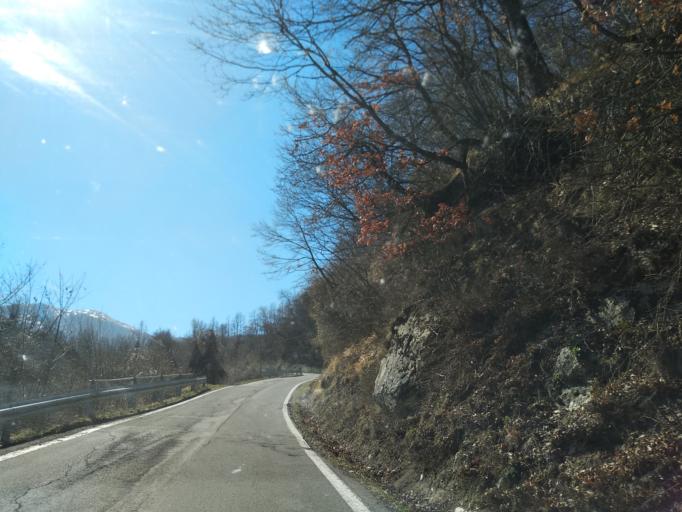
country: IT
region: Emilia-Romagna
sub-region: Provincia di Reggio Emilia
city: Ramiseto
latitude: 44.4080
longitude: 10.2720
